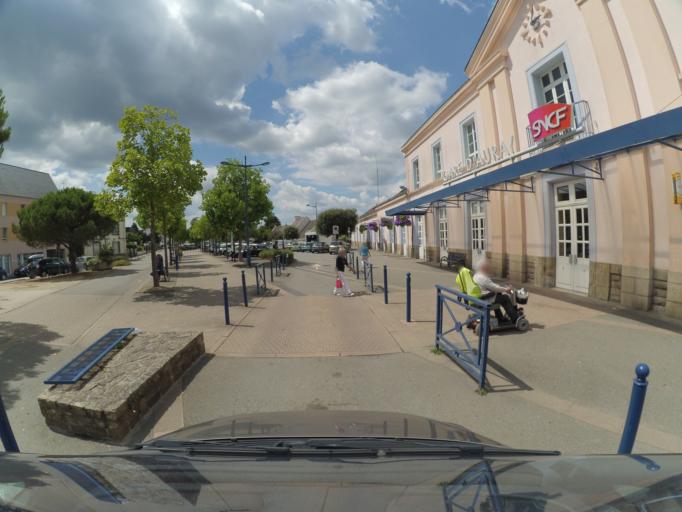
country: FR
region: Brittany
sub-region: Departement du Morbihan
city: Auray
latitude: 47.6800
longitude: -2.9994
